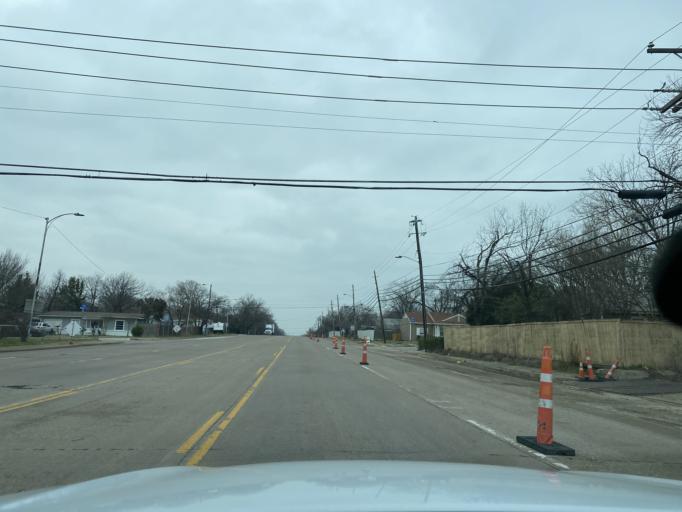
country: US
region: Texas
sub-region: Tarrant County
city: Arlington
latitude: 32.7152
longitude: -97.0975
